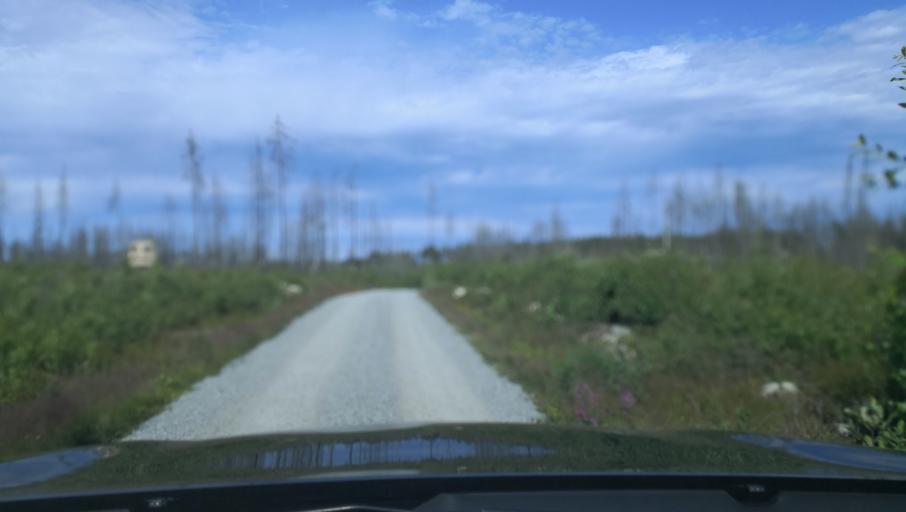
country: SE
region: Vaestmanland
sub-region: Surahammars Kommun
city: Ramnas
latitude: 59.9323
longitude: 16.1891
